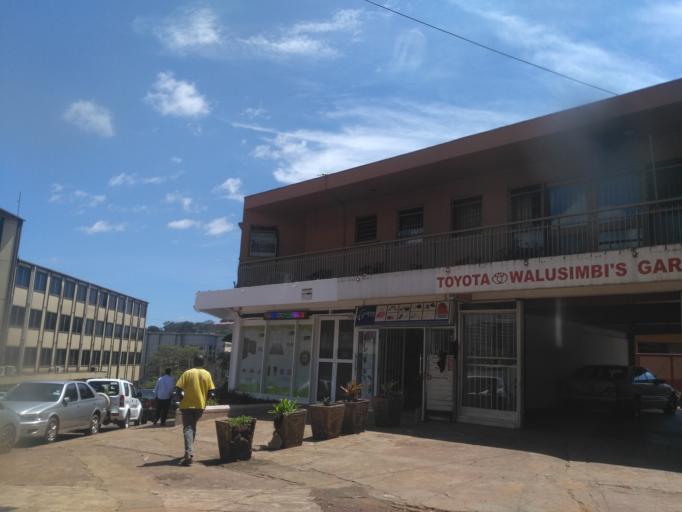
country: UG
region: Central Region
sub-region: Kampala District
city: Kampala
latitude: 0.3161
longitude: 32.5909
